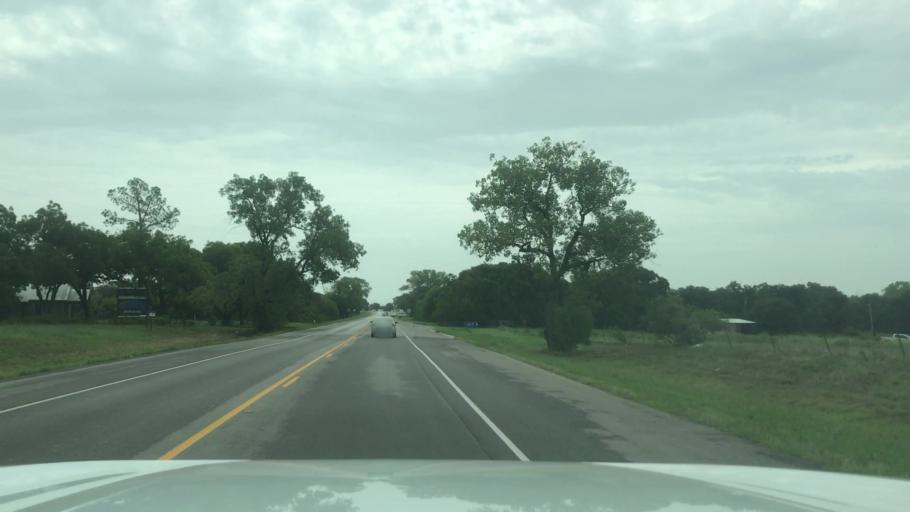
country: US
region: Texas
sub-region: Eastland County
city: Gorman
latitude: 32.2202
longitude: -98.6786
